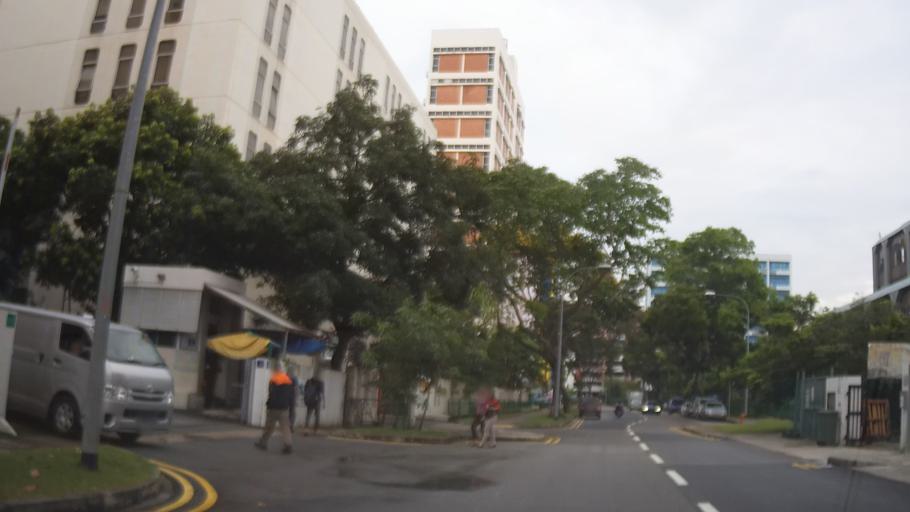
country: SG
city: Singapore
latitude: 1.3278
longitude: 103.8773
